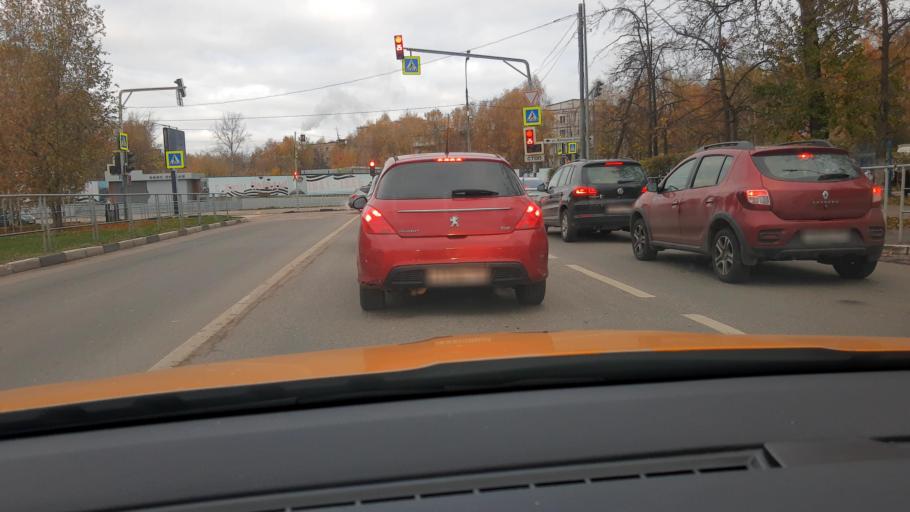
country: RU
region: Moskovskaya
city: Odintsovo
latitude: 55.6803
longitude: 37.2651
